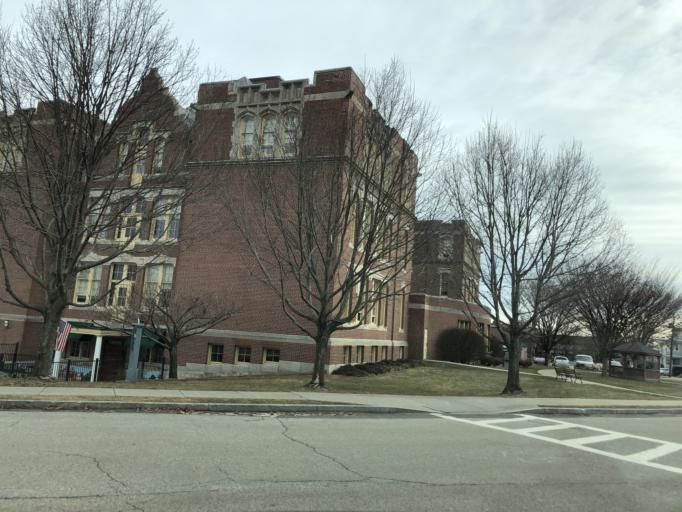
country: US
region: Massachusetts
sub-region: Middlesex County
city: Watertown
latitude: 42.3685
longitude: -71.1700
